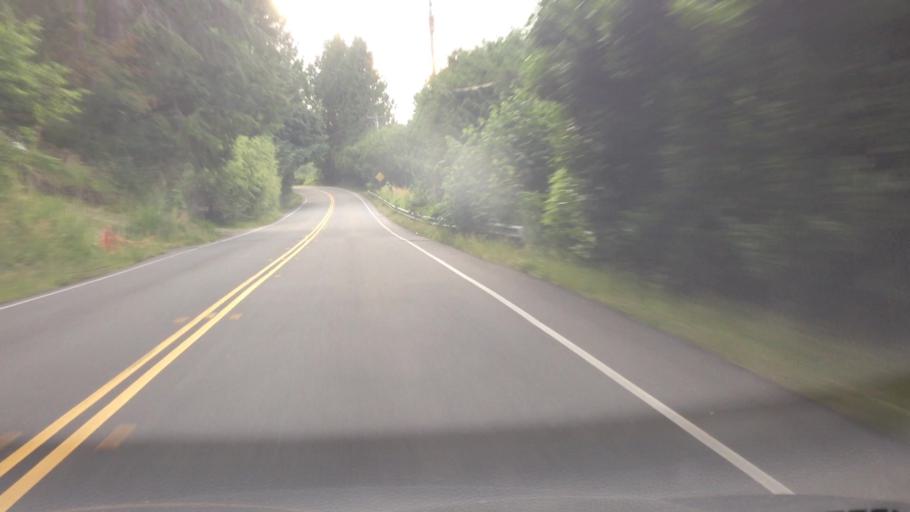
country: US
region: Washington
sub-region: King County
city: Duvall
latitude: 47.7459
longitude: -121.9557
